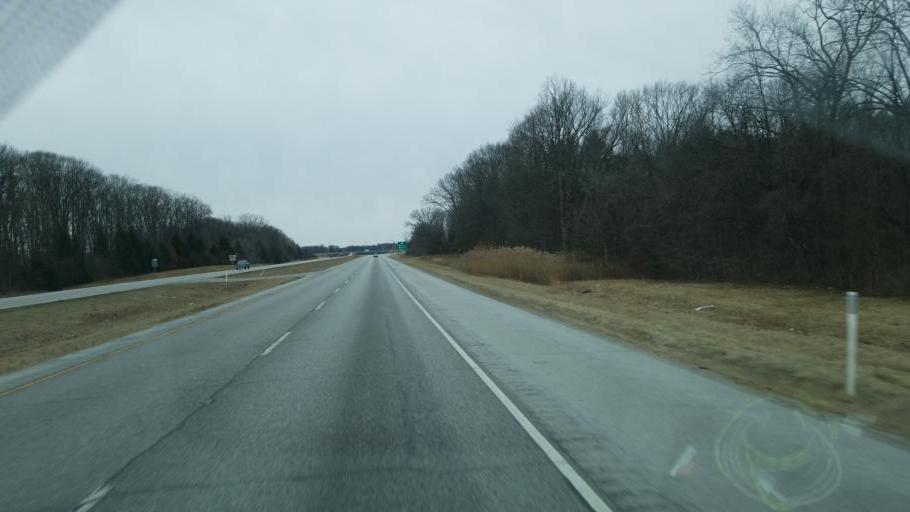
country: US
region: Indiana
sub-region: Porter County
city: Chesterton
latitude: 41.5598
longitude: -87.0468
